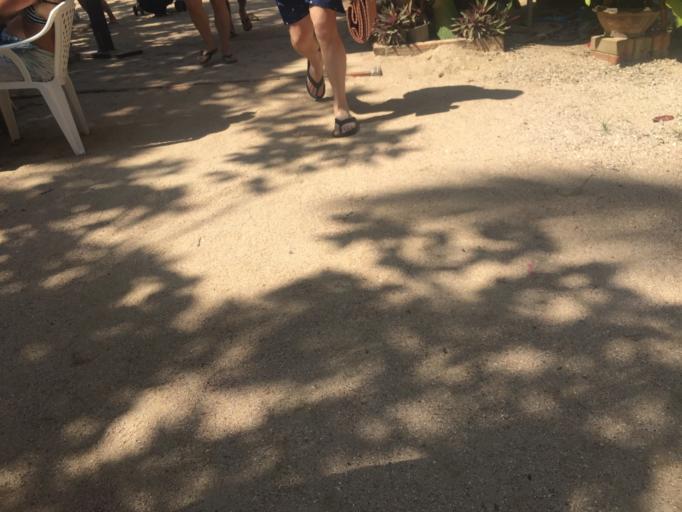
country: TH
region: Phangnga
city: Ban Ao Nang
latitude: 8.0286
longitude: 98.8250
